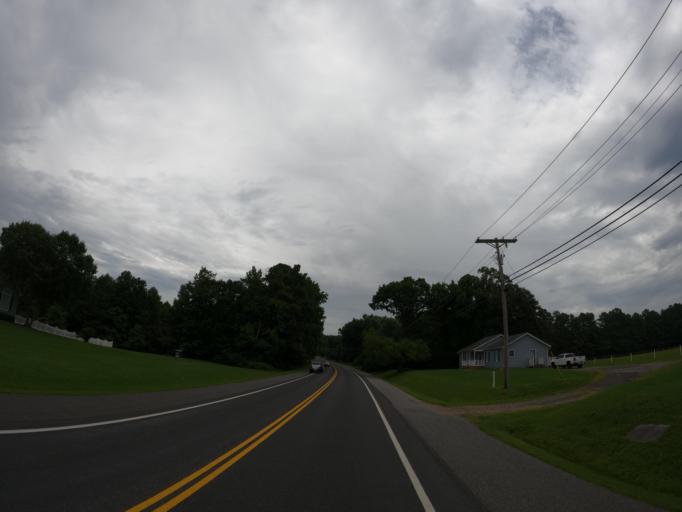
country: US
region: Maryland
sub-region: Saint Mary's County
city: Lexington Park
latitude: 38.2033
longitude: -76.5105
